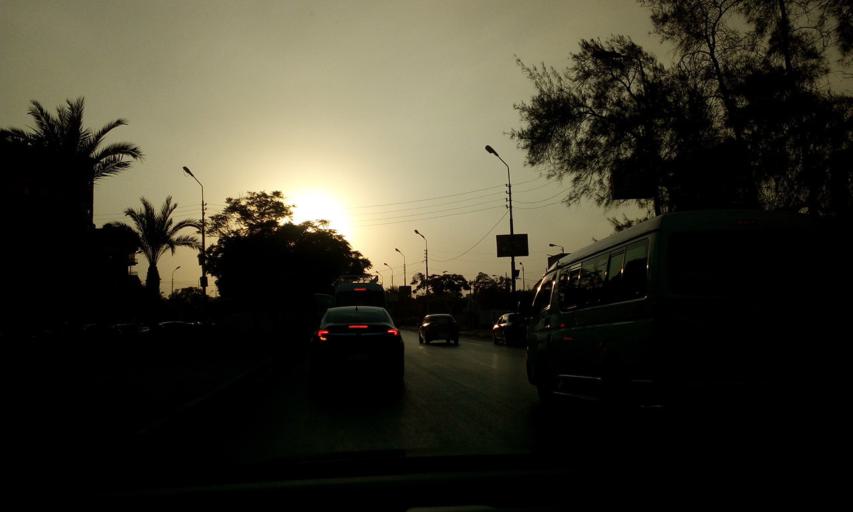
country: EG
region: Muhafazat al Qalyubiyah
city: Al Khankah
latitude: 30.1193
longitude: 31.3536
